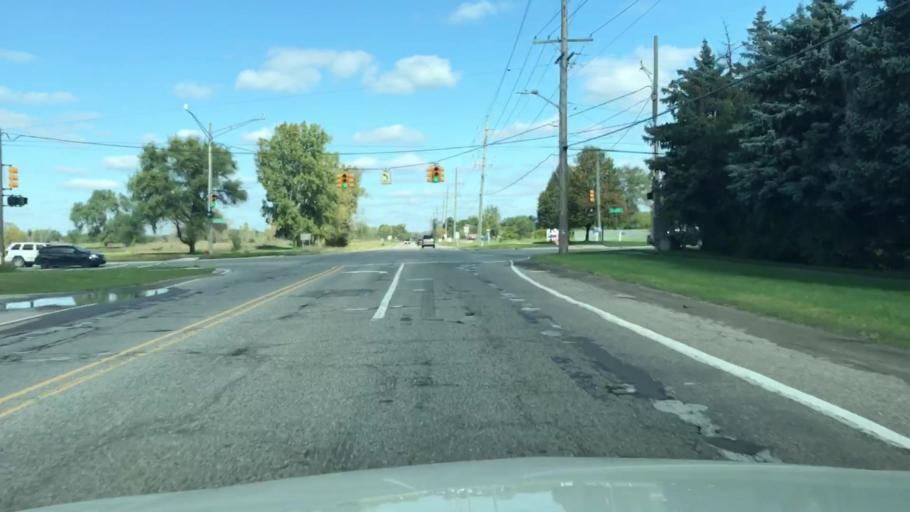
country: US
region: Michigan
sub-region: Oakland County
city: Rochester
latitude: 42.6527
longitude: -83.0928
